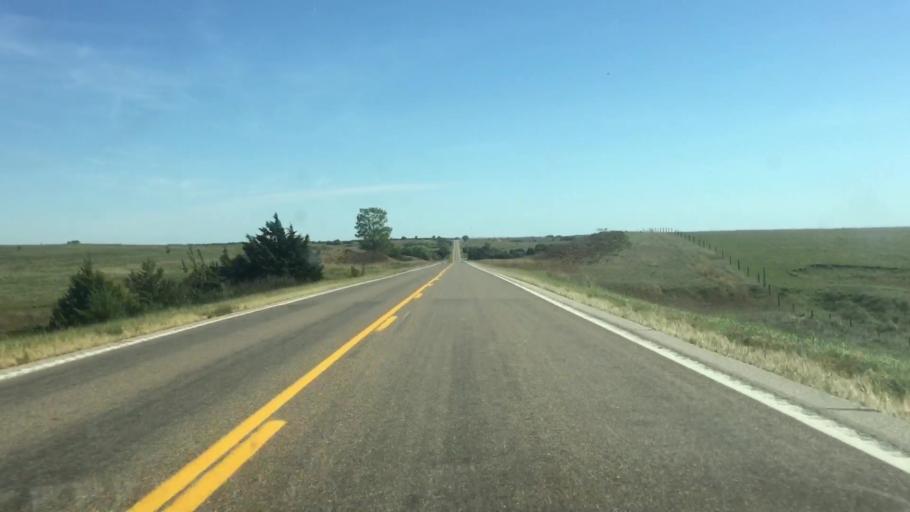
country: US
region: Nebraska
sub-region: Thayer County
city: Hebron
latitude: 40.1472
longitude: -97.5338
